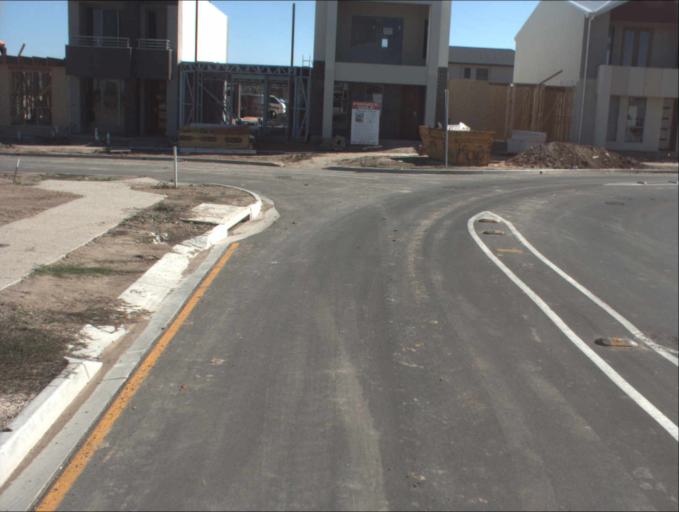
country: AU
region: South Australia
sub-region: Port Adelaide Enfield
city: Klemzig
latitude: -34.8636
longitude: 138.6302
